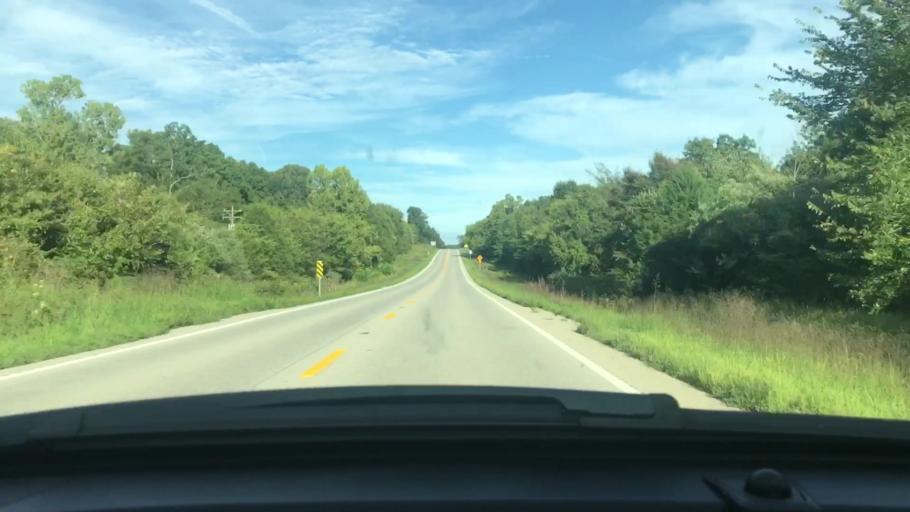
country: US
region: Arkansas
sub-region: Sharp County
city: Cherokee Village
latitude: 36.2745
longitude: -91.3467
